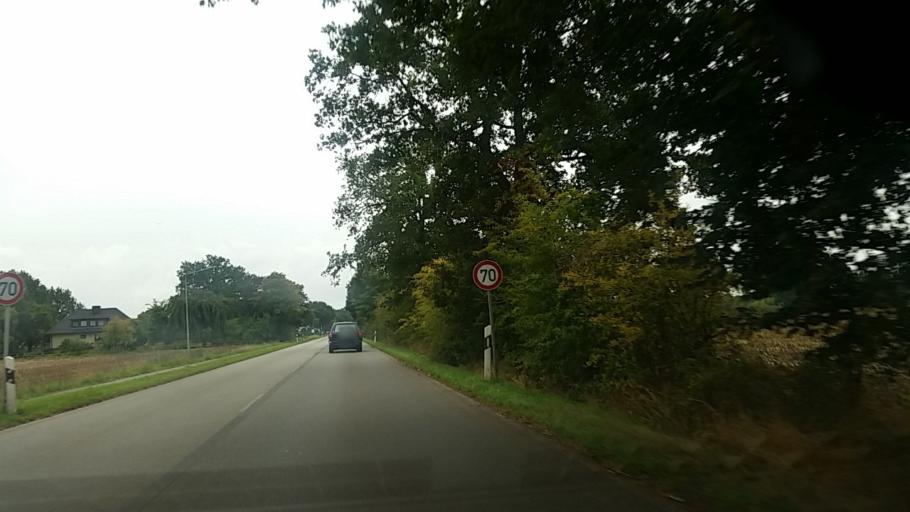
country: DE
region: Schleswig-Holstein
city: Kayhude
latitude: 53.7642
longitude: 10.1276
